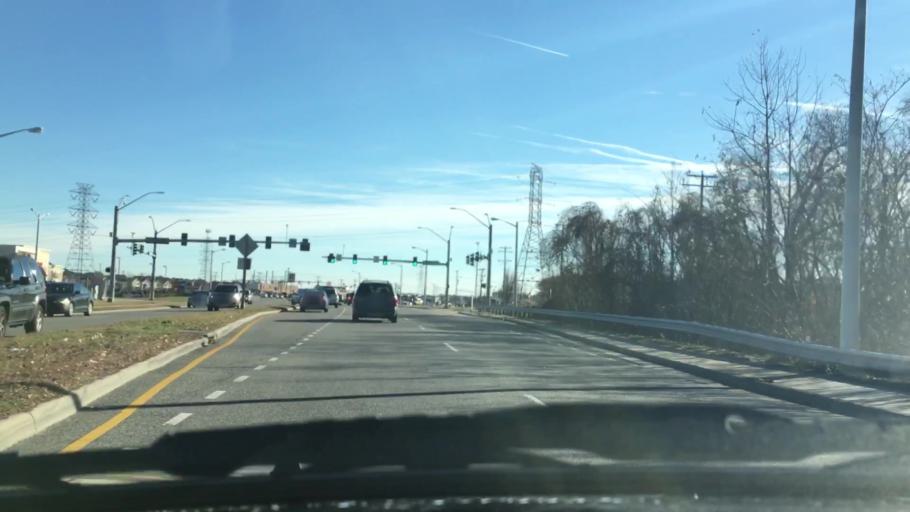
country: US
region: Virginia
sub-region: City of Portsmouth
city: Portsmouth Heights
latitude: 36.8806
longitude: -76.4251
